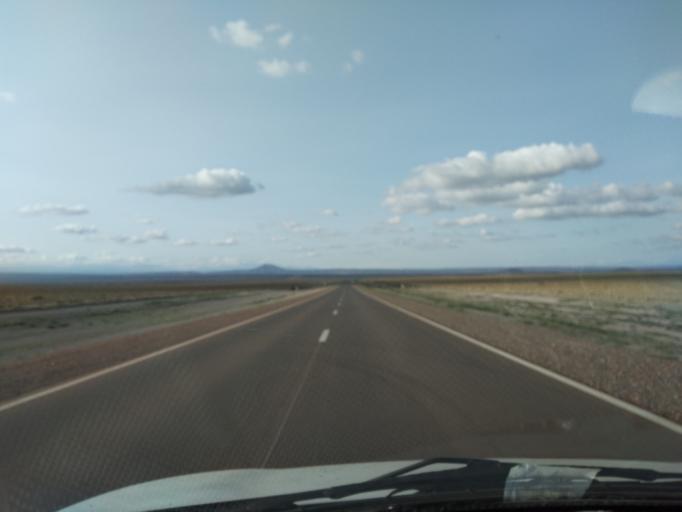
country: AR
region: Mendoza
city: San Rafael
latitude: -34.6776
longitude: -69.1591
